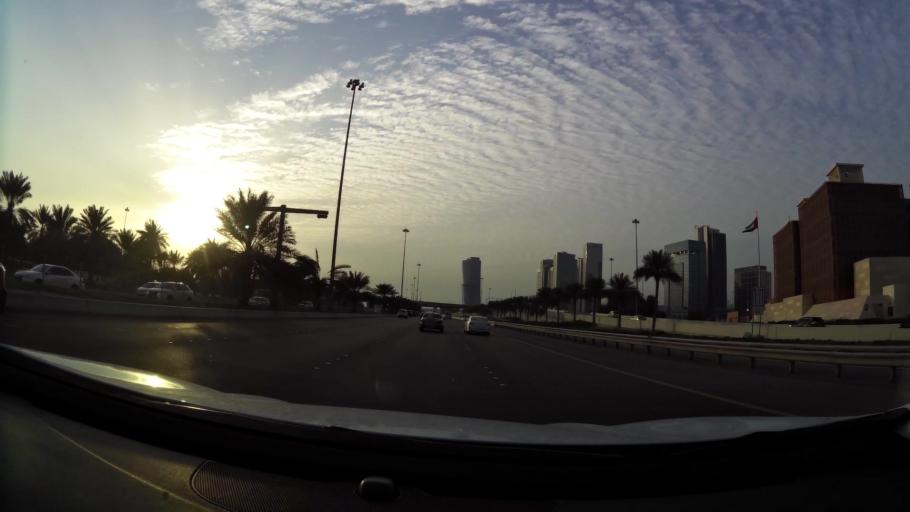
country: AE
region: Abu Dhabi
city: Abu Dhabi
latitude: 24.4146
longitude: 54.4463
